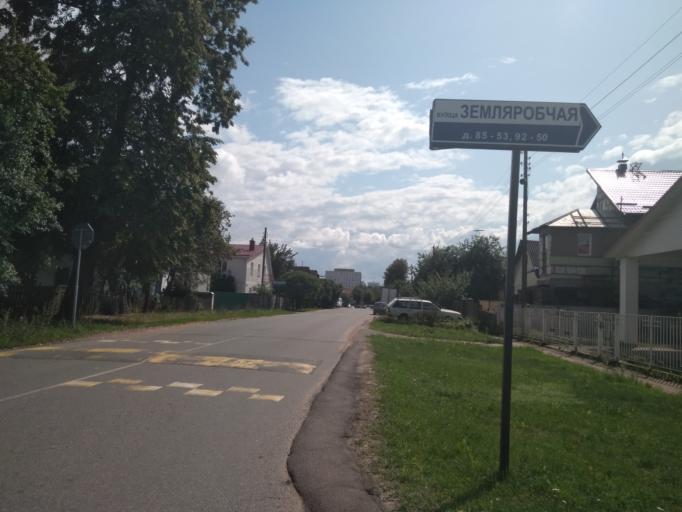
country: BY
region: Minsk
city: Minsk
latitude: 53.9379
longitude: 27.5558
